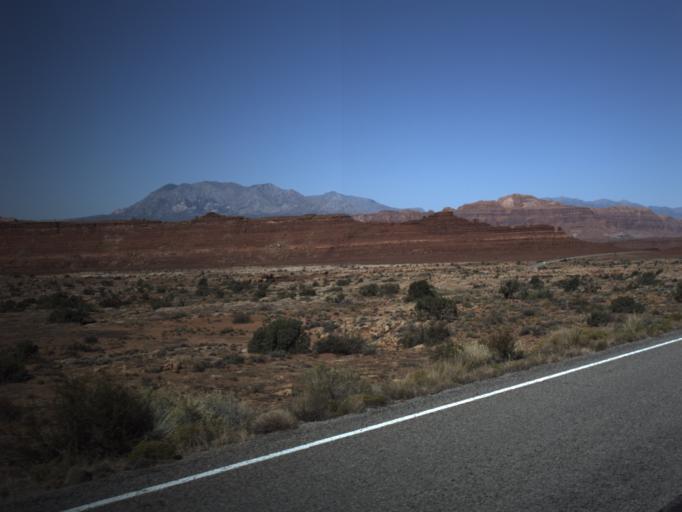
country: US
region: Utah
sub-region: San Juan County
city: Blanding
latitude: 37.8156
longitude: -110.3444
